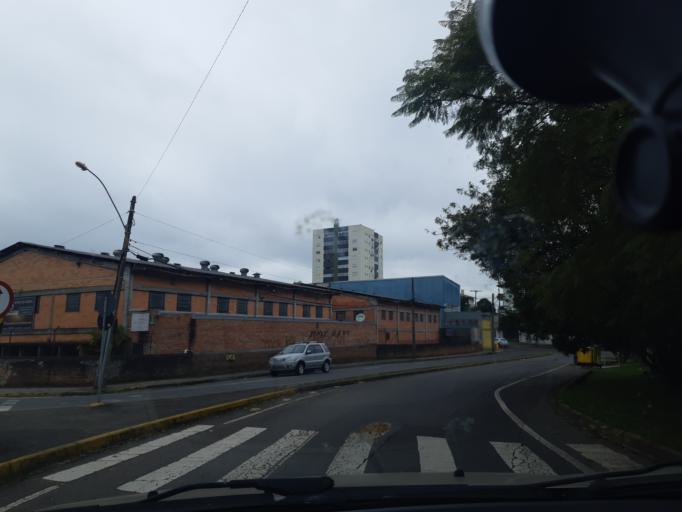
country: BR
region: Rio Grande do Sul
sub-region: Caxias Do Sul
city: Caxias do Sul
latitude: -29.1538
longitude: -51.2070
